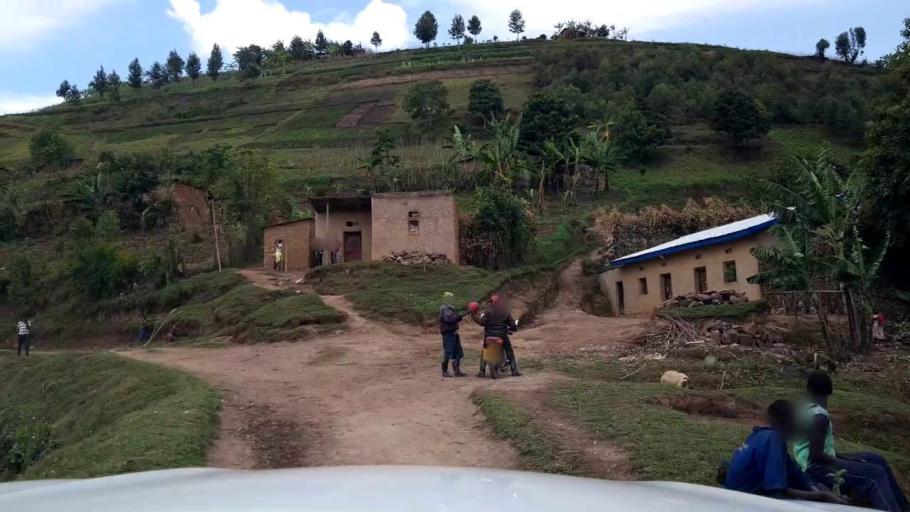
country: RW
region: Northern Province
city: Byumba
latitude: -1.5265
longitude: 30.1308
